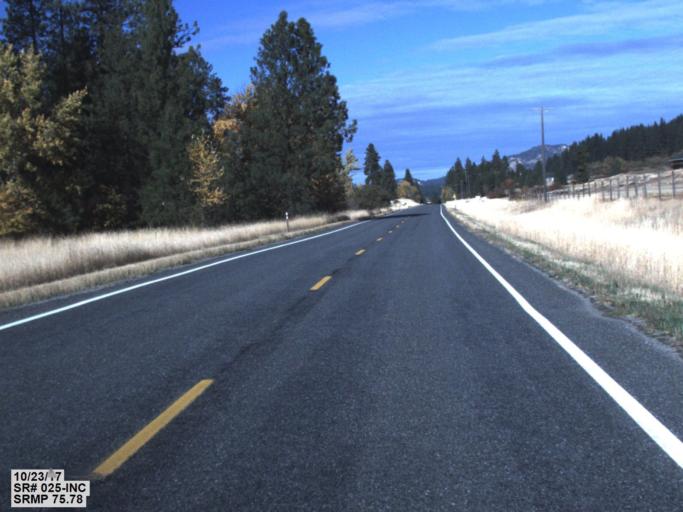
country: US
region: Washington
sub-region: Stevens County
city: Kettle Falls
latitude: 48.5516
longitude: -118.1264
